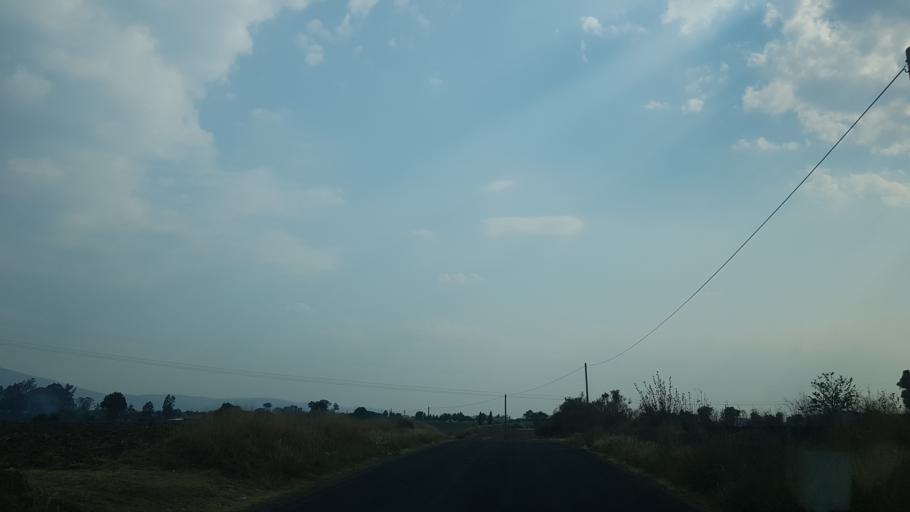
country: MX
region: Puebla
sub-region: Santa Isabel Cholula
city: Santa Ana Acozautla
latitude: 18.9549
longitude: -98.3941
